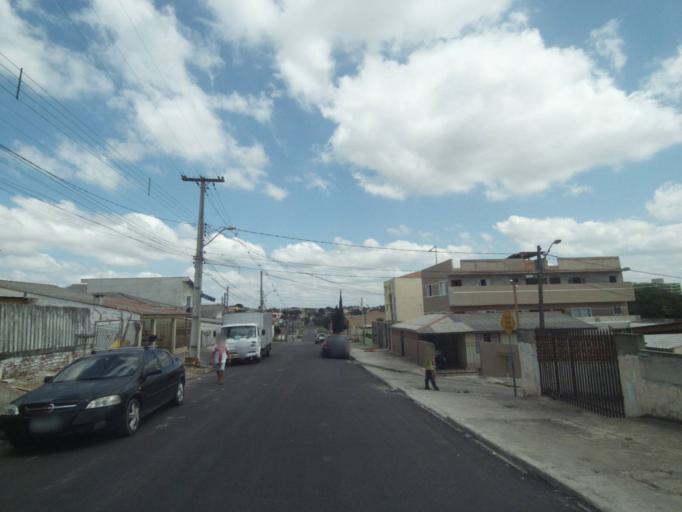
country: BR
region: Parana
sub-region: Curitiba
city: Curitiba
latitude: -25.5054
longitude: -49.3064
